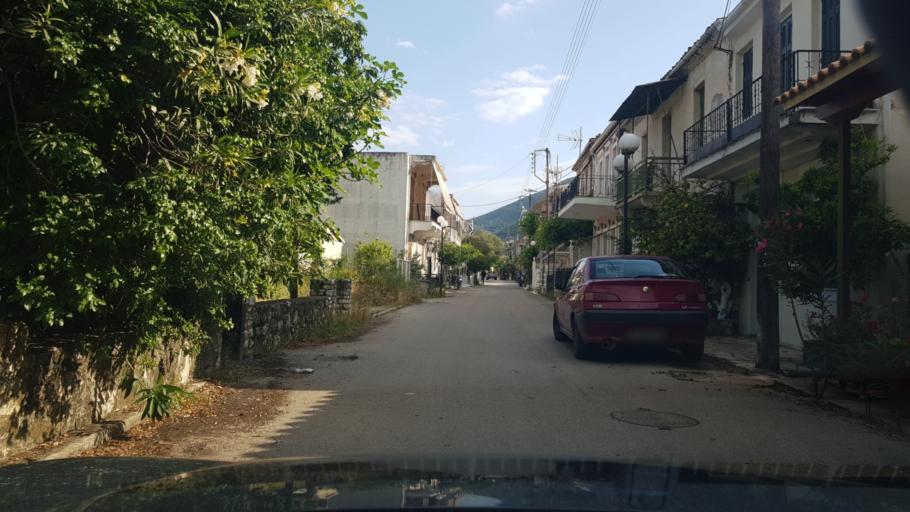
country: GR
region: Ionian Islands
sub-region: Lefkada
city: Nidri
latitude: 38.6827
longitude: 20.6981
